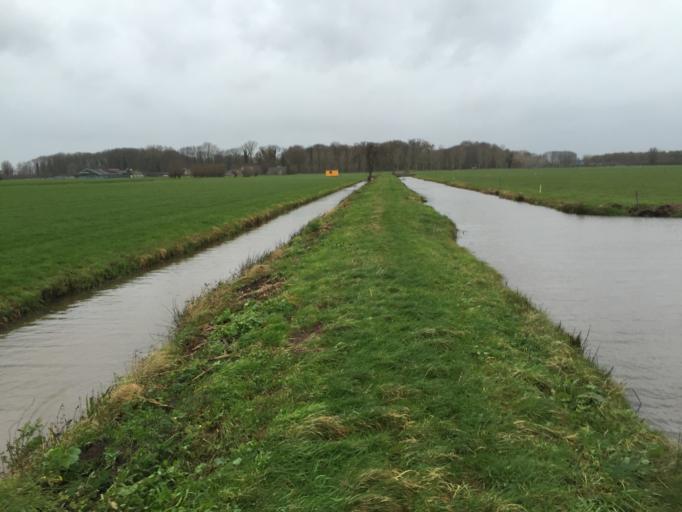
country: NL
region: Utrecht
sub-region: Gemeente Montfoort
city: Montfoort
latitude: 52.0495
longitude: 4.9108
